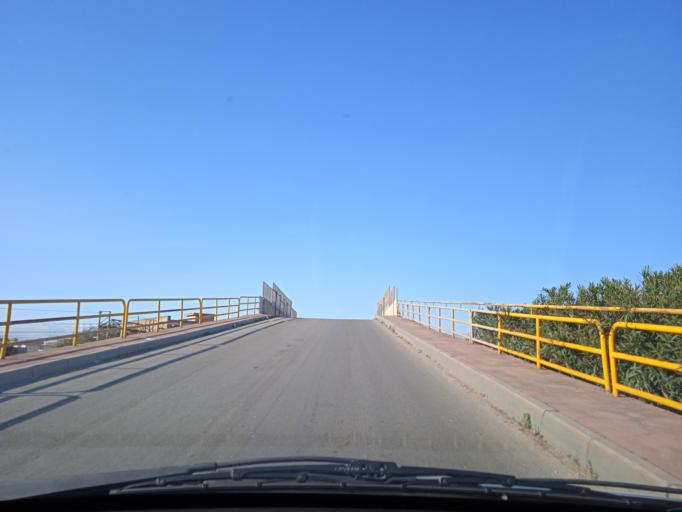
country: IT
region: Sicily
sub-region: Palermo
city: Villabate
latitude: 38.0860
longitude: 13.4499
